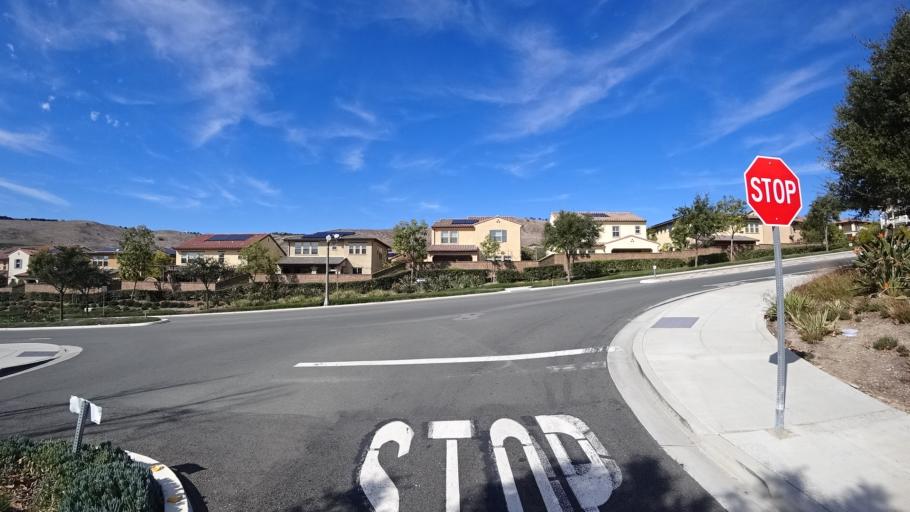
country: US
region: California
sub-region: Orange County
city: Ladera Ranch
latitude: 33.5273
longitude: -117.6230
